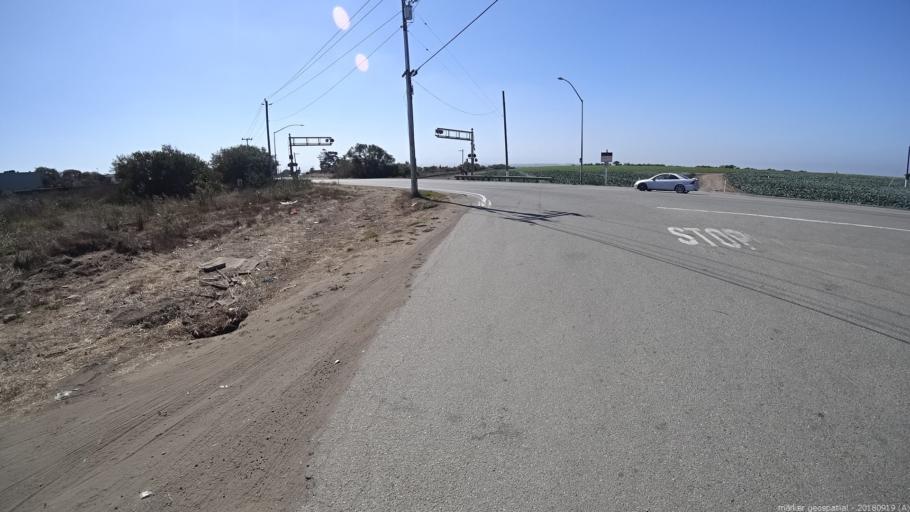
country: US
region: California
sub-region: Monterey County
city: Castroville
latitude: 36.7553
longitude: -121.7437
